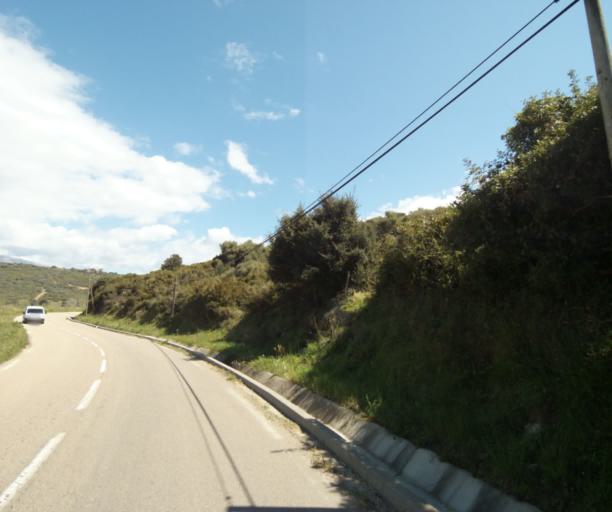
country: FR
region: Corsica
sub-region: Departement de la Corse-du-Sud
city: Propriano
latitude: 41.6573
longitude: 8.8961
